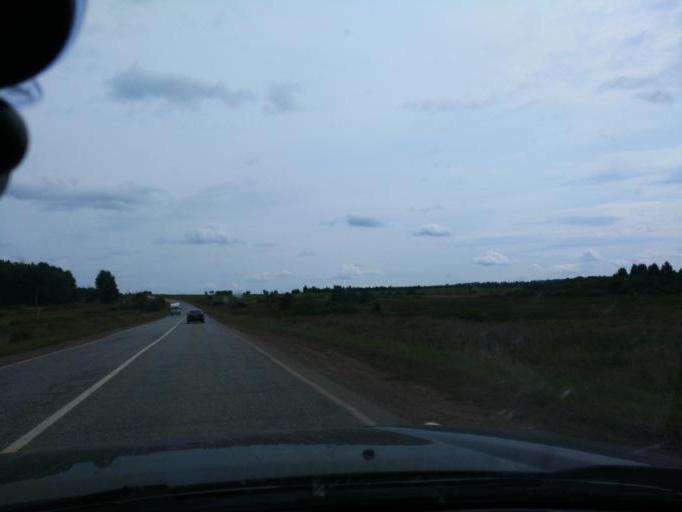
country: RU
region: Perm
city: Kuyeda
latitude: 56.4693
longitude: 55.7227
